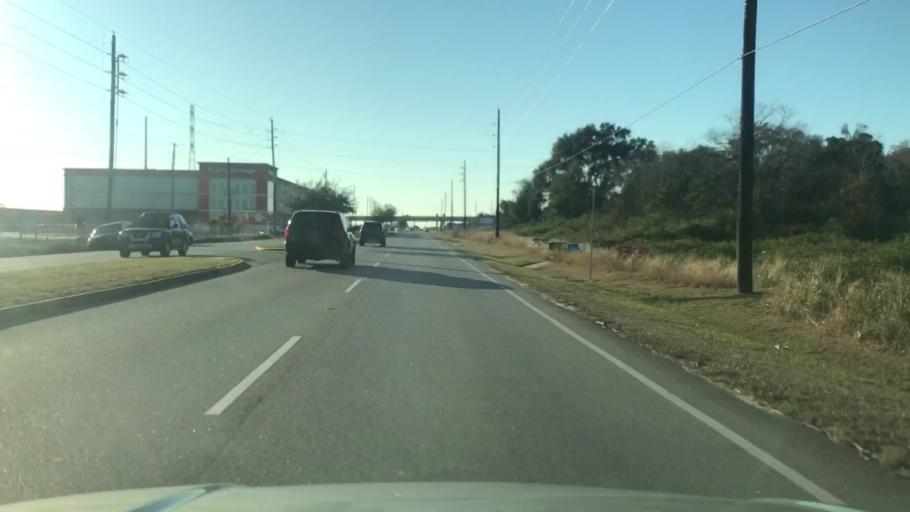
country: US
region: Texas
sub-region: Harris County
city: Katy
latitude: 29.8317
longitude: -95.7554
